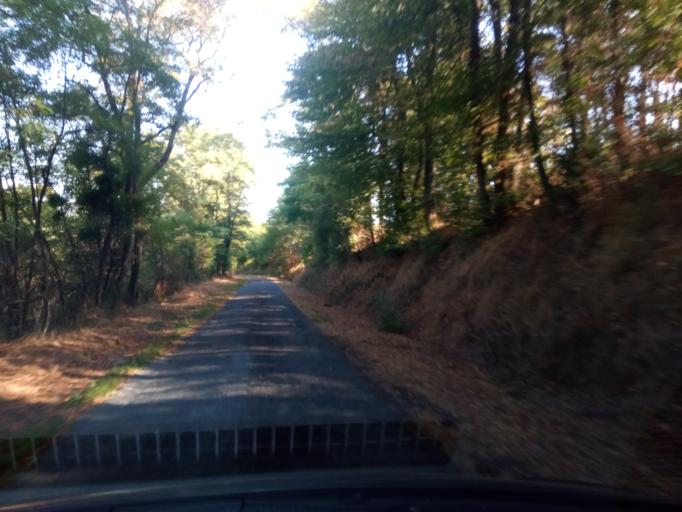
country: FR
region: Poitou-Charentes
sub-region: Departement de la Vienne
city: Saulge
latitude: 46.3751
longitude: 0.8719
